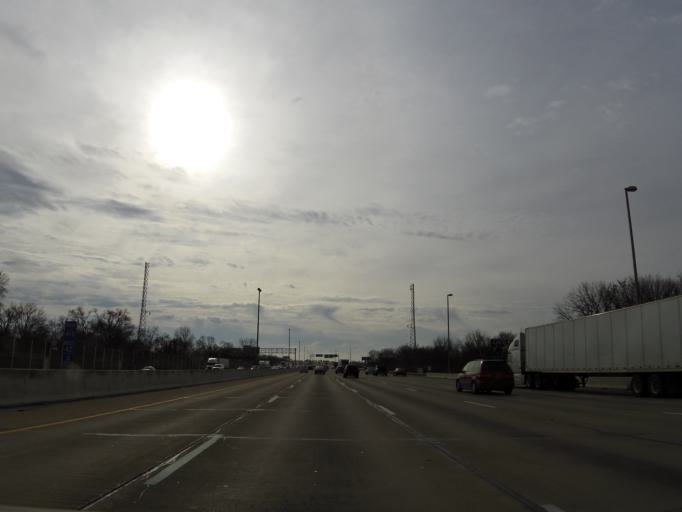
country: US
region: Indiana
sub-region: Marion County
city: Lawrence
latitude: 39.8166
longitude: -86.0311
